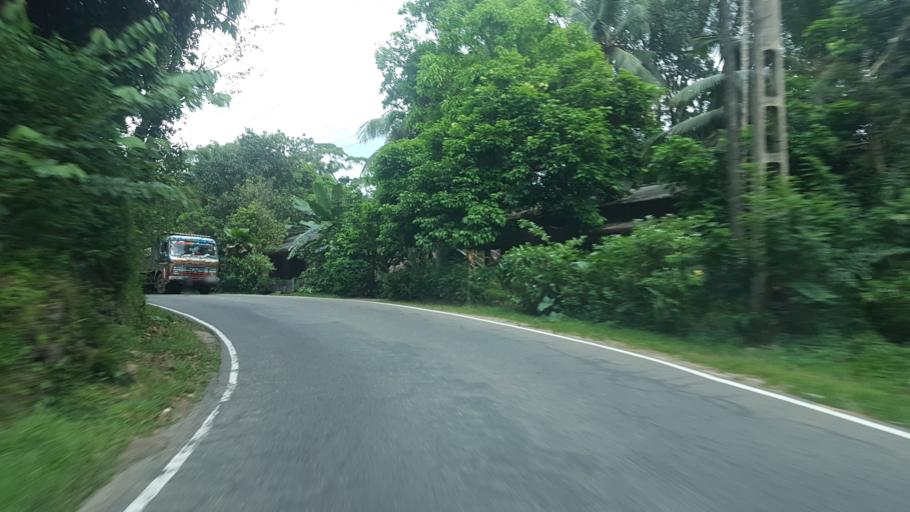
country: LK
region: Western
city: Hanwella Ihala
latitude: 7.0269
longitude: 80.2794
